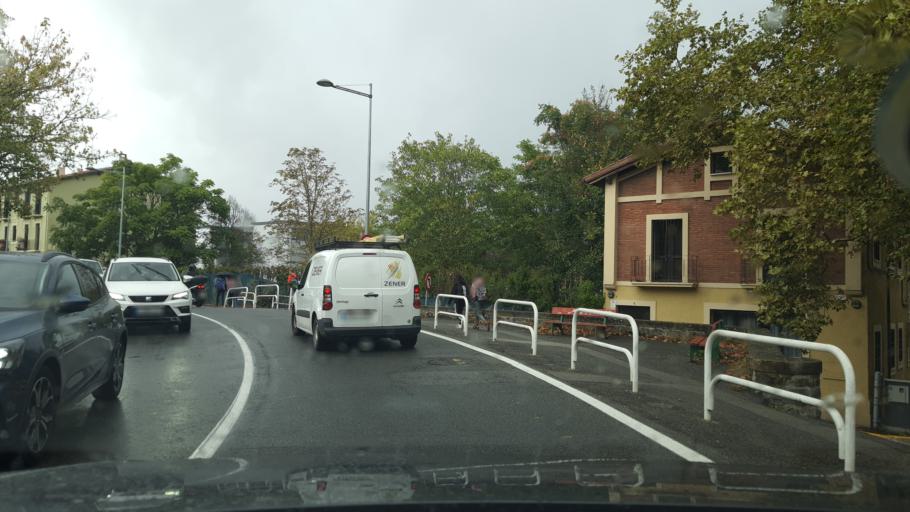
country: ES
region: Navarre
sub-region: Provincia de Navarra
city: Pamplona
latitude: 42.8223
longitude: -1.6401
